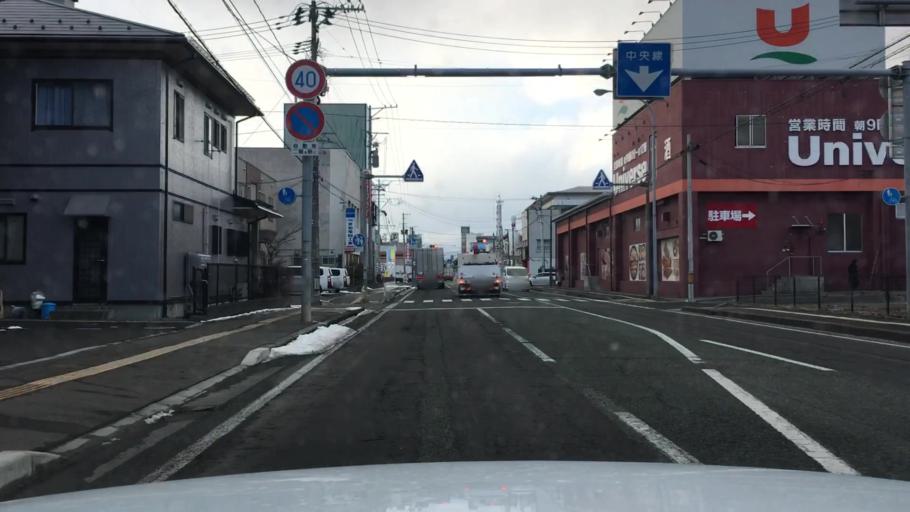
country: JP
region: Iwate
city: Morioka-shi
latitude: 39.6918
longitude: 141.1724
